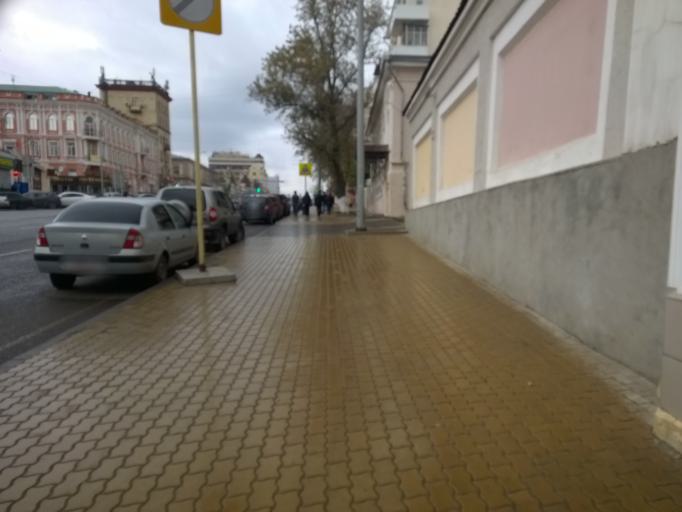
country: RU
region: Rostov
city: Rostov-na-Donu
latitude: 47.2180
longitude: 39.7208
